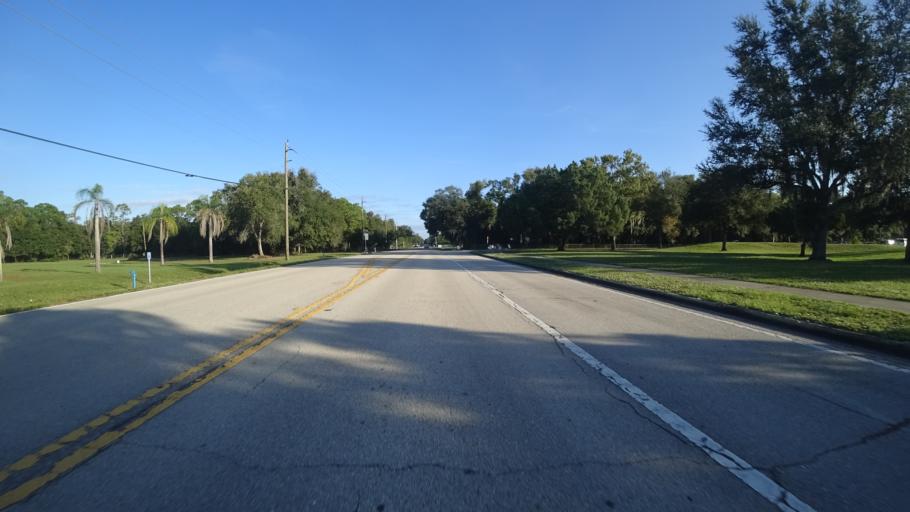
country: US
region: Florida
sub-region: Manatee County
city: Samoset
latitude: 27.4682
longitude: -82.4893
